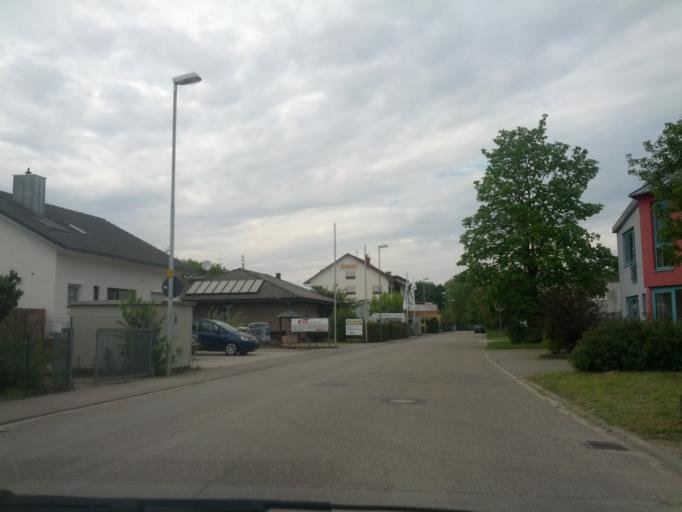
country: DE
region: Baden-Wuerttemberg
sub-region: Freiburg Region
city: Teningen
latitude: 48.1094
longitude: 7.7832
